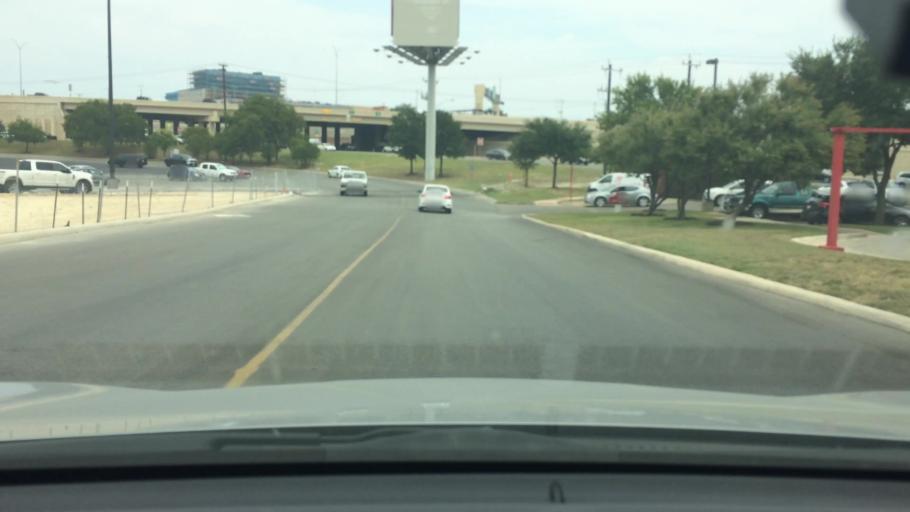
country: US
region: Texas
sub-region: Bexar County
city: Leon Valley
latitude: 29.4666
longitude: -98.6212
